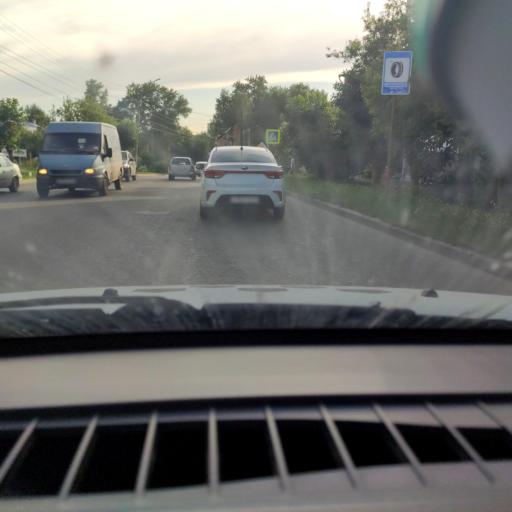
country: RU
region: Kirov
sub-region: Kirovo-Chepetskiy Rayon
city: Kirov
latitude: 58.6228
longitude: 49.6423
